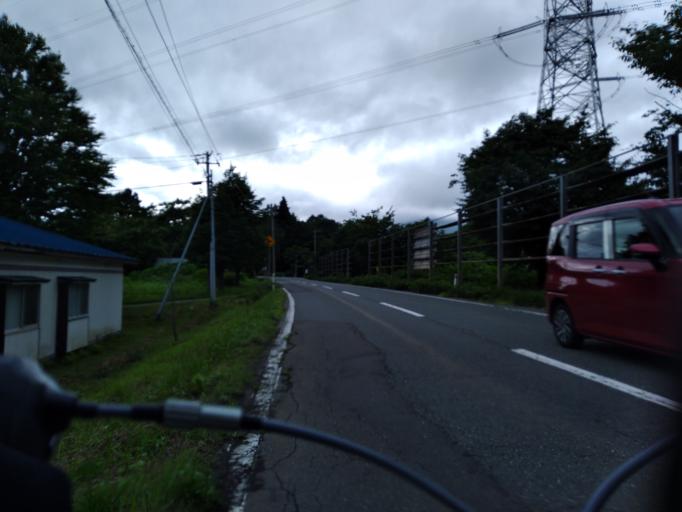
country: JP
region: Iwate
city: Morioka-shi
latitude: 39.8122
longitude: 141.0762
